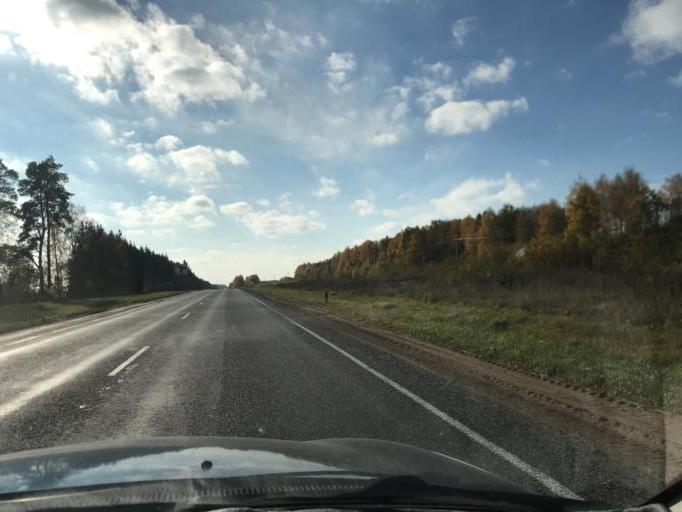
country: BY
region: Grodnenskaya
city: Voranava
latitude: 54.2152
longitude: 25.3530
